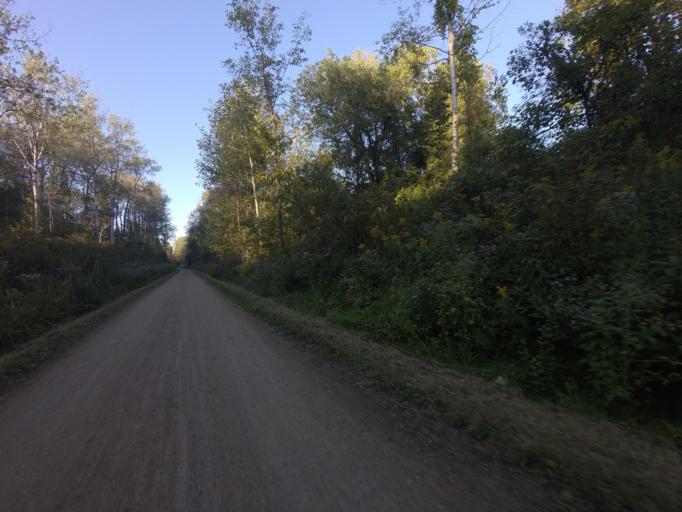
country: CA
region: Ontario
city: Brampton
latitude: 43.8523
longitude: -79.8775
